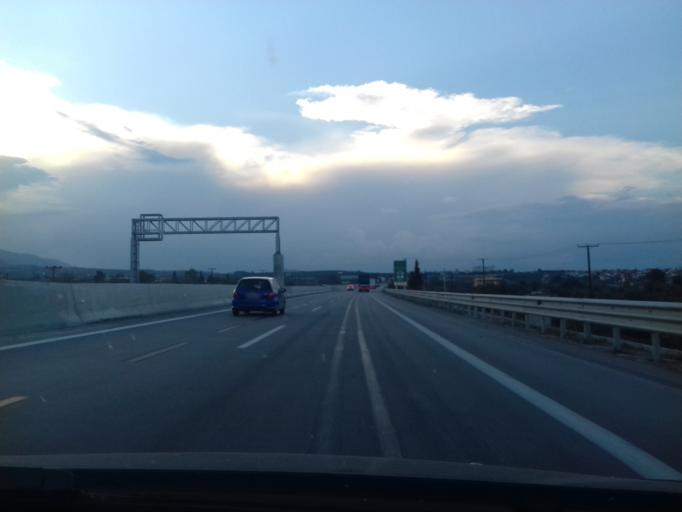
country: GR
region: West Greece
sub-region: Nomos Achaias
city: Aigio
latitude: 38.2293
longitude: 22.0869
